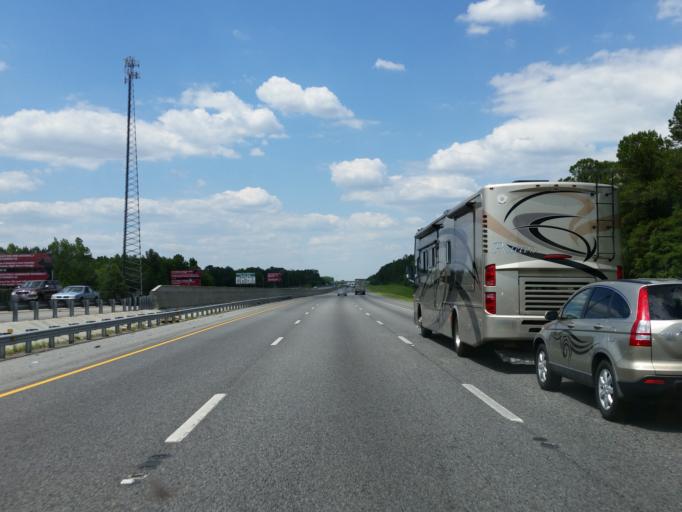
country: US
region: Georgia
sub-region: Lowndes County
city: Hahira
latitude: 30.9367
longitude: -83.3708
